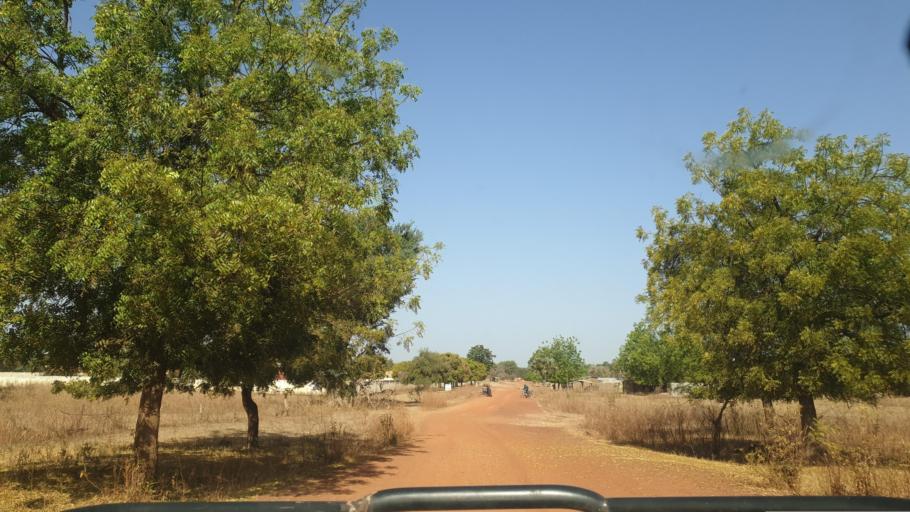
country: ML
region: Sikasso
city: Bougouni
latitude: 11.8119
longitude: -6.9342
